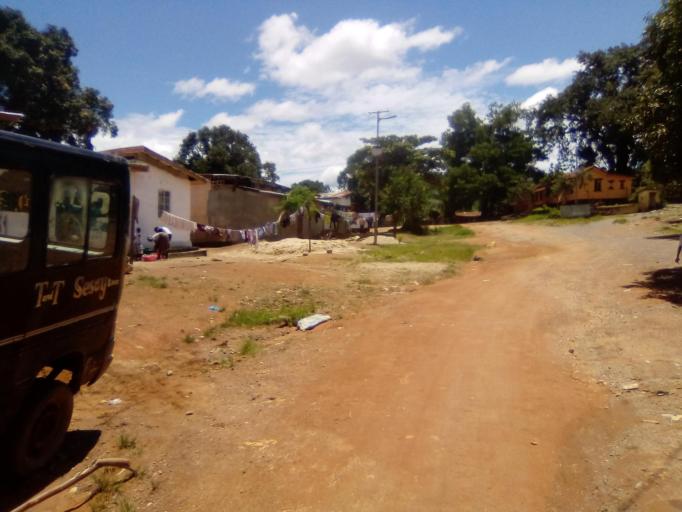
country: SL
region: Eastern Province
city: Koidu
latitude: 8.6377
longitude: -10.9747
